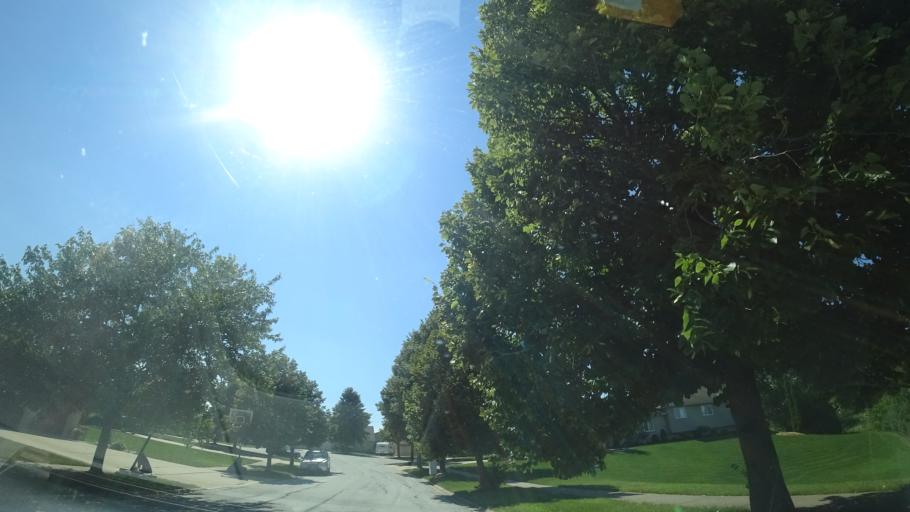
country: US
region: Illinois
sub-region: Will County
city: Mokena
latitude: 41.5650
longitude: -87.9051
